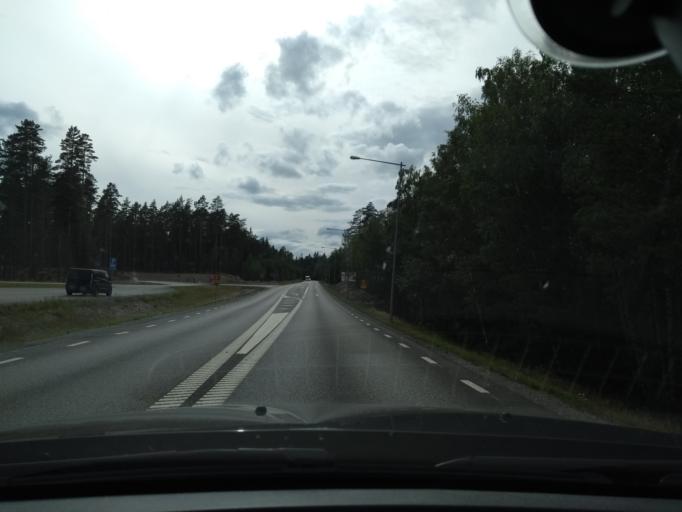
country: SE
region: Joenkoeping
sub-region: Eksjo Kommun
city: Mariannelund
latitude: 57.6228
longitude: 15.5968
